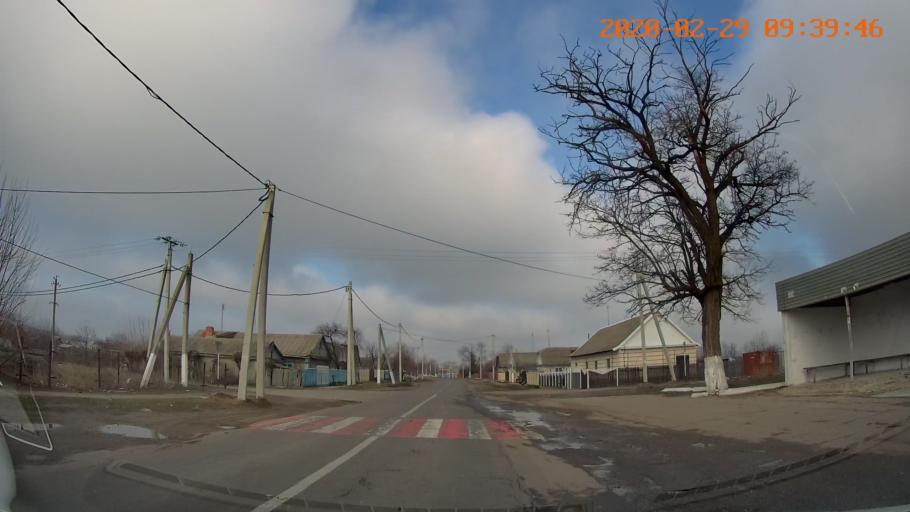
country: MD
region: Telenesti
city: Crasnoe
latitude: 46.6371
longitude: 29.8510
